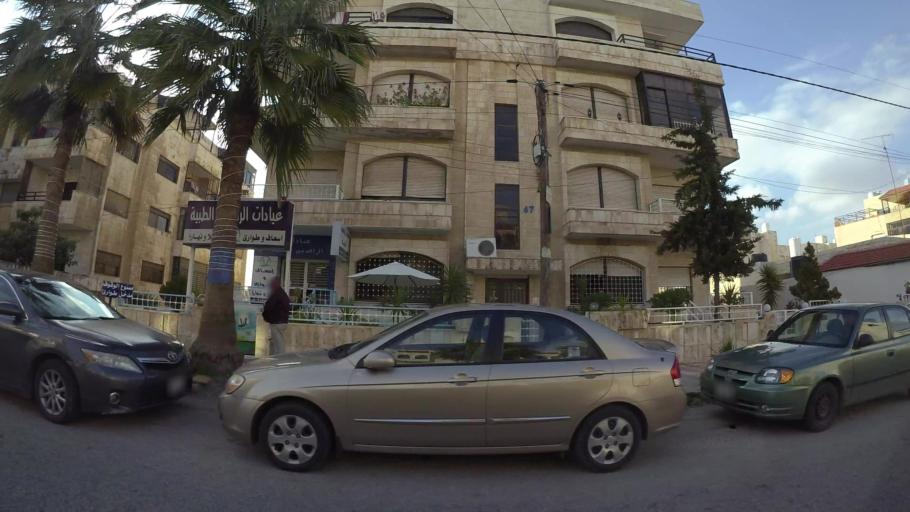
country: JO
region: Amman
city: Al Jubayhah
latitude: 31.9880
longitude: 35.8716
